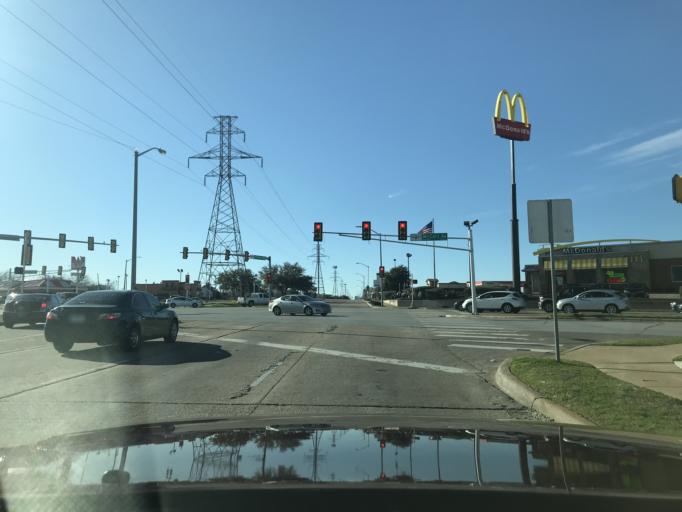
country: US
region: Texas
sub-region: Tarrant County
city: Edgecliff Village
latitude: 32.6499
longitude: -97.3668
